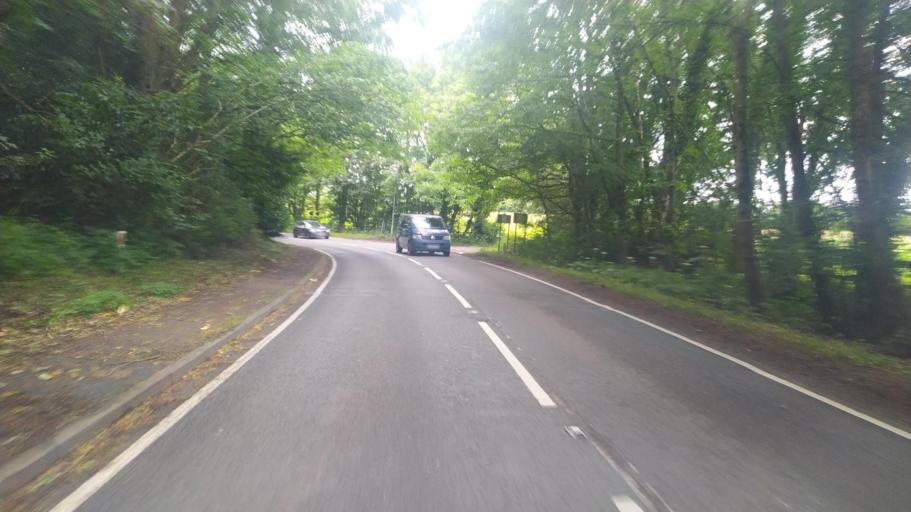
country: GB
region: England
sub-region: Hampshire
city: Liphook
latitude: 51.0867
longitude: -0.8095
